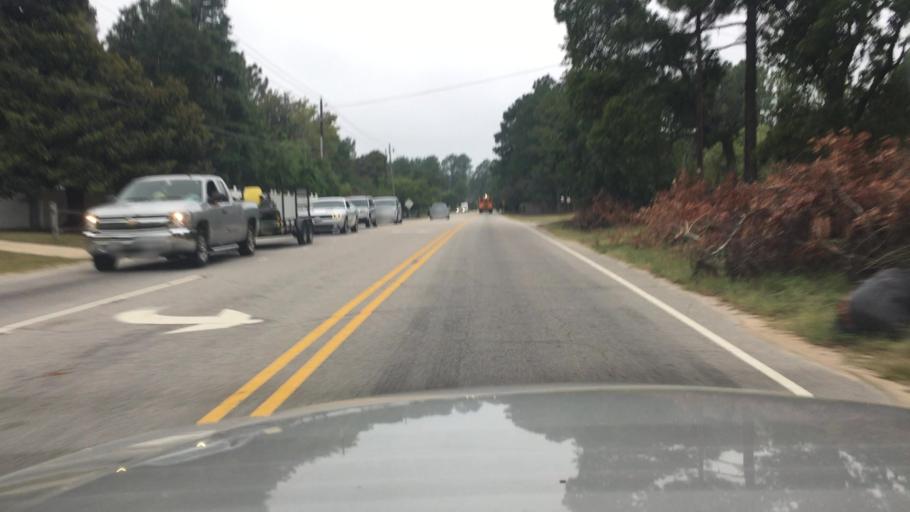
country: US
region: North Carolina
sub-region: Cumberland County
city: Hope Mills
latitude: 34.9727
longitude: -78.9601
